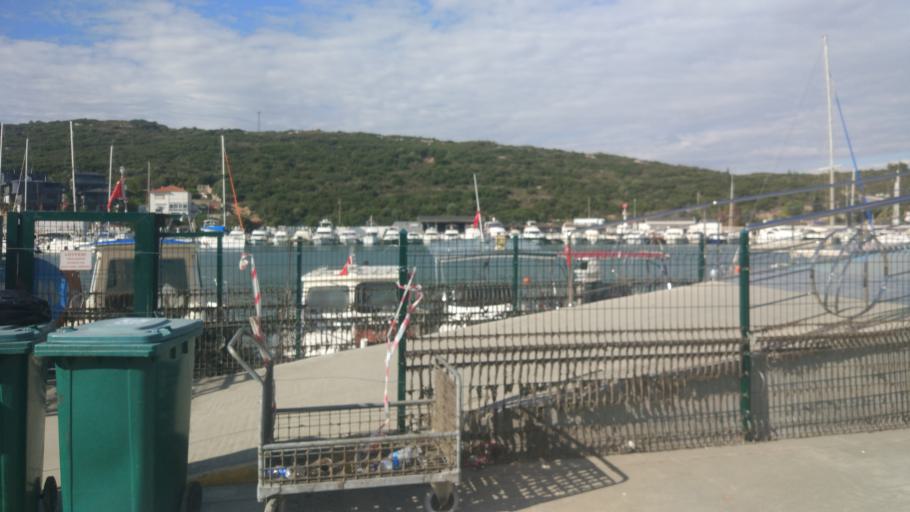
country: TR
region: Izmir
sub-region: Seferihisar
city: Seferhisar
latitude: 38.1928
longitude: 26.7834
